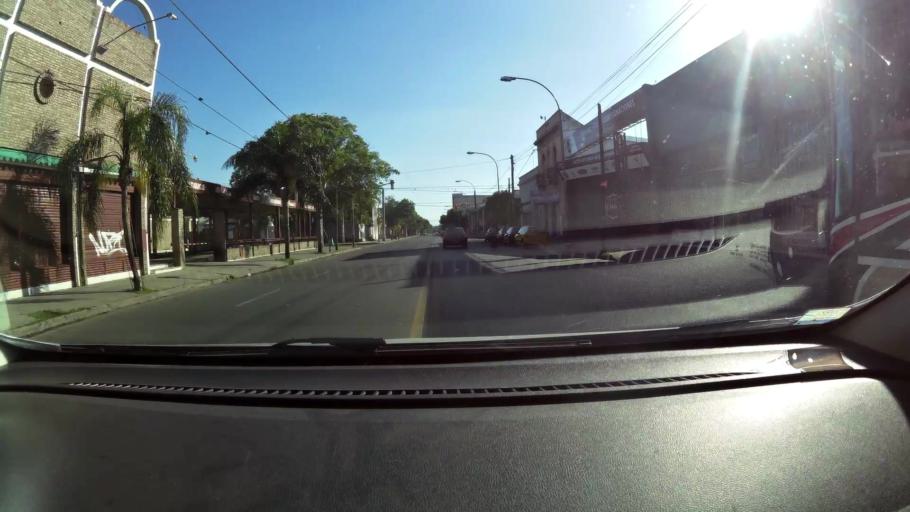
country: AR
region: Cordoba
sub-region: Departamento de Capital
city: Cordoba
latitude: -31.3948
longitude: -64.1673
